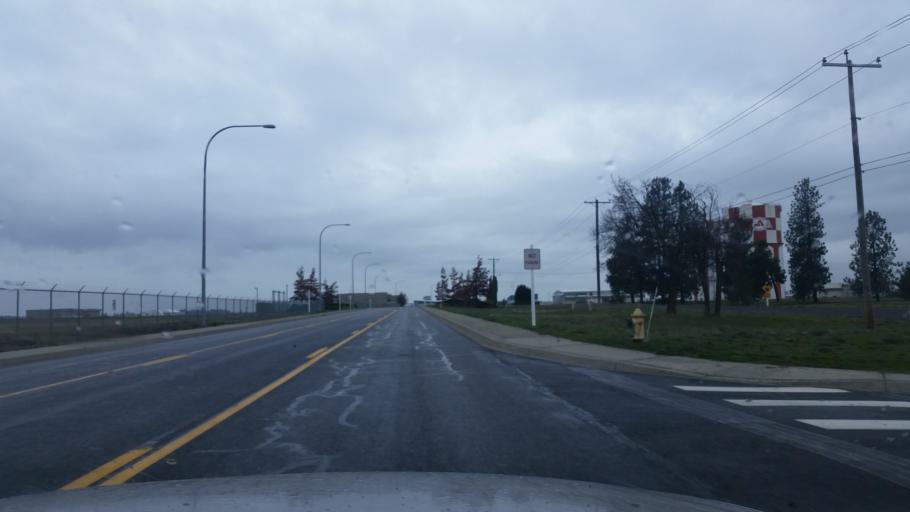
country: US
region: Washington
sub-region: Spokane County
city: Airway Heights
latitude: 47.6191
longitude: -117.5158
